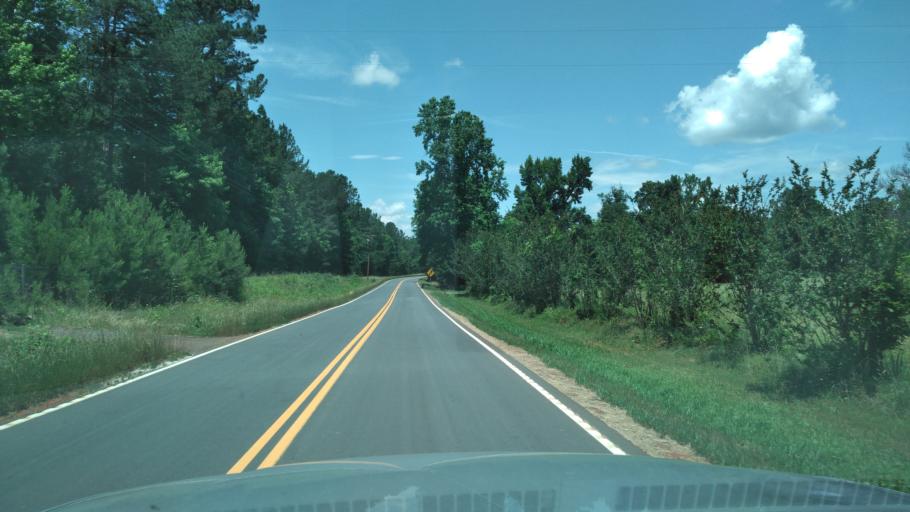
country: US
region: South Carolina
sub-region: Greenwood County
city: Ware Shoals
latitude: 34.4169
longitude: -82.1320
